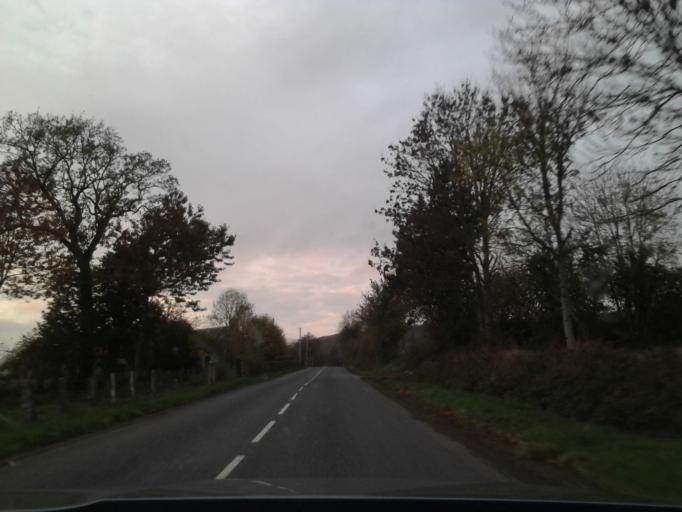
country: FR
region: Lower Normandy
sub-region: Departement du Calvados
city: Saint-Martin-des-Besaces
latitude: 48.9308
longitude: -0.8151
